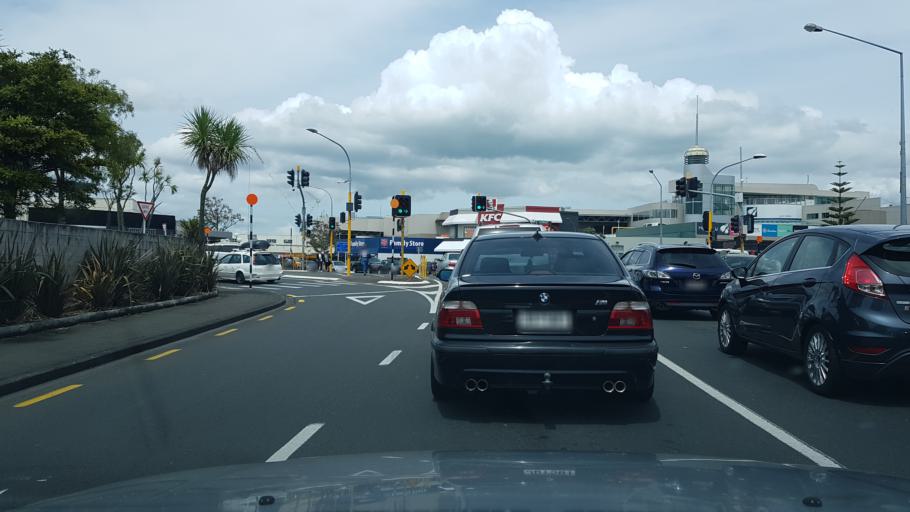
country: NZ
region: Auckland
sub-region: Auckland
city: North Shore
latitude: -36.8096
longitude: 174.7256
